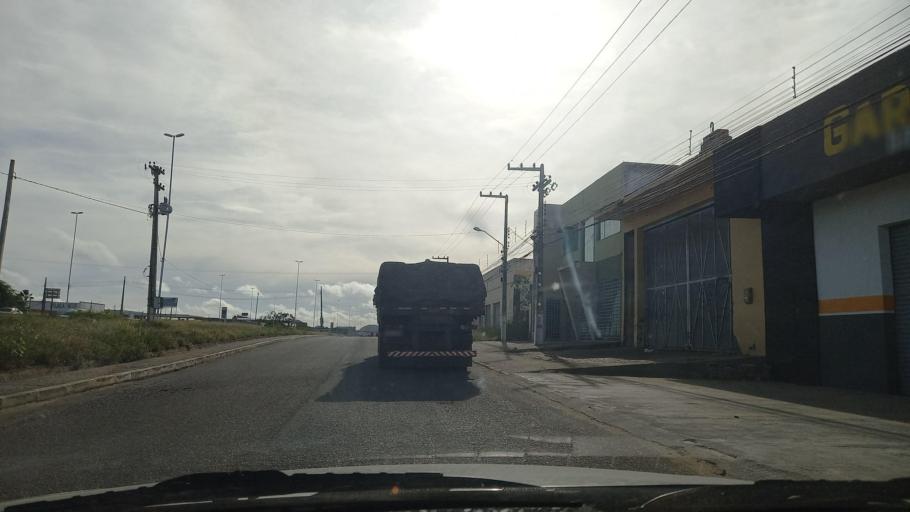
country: BR
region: Pernambuco
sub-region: Bezerros
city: Bezerros
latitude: -8.2414
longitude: -35.7496
